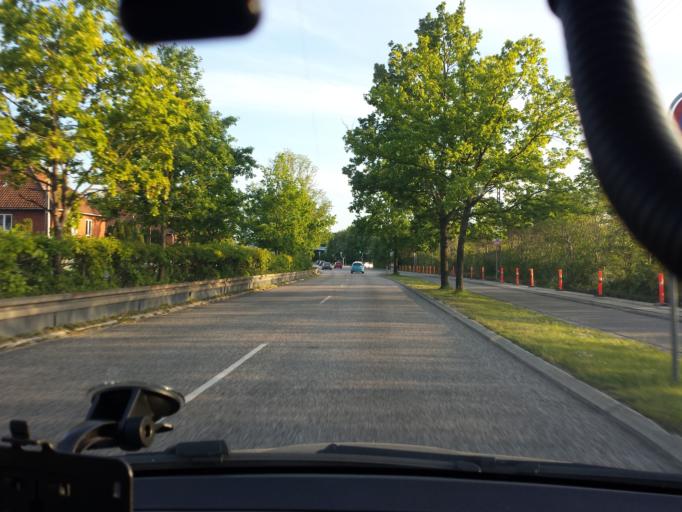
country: DK
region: Capital Region
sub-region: Herlev Kommune
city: Herlev
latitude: 55.7287
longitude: 12.4436
